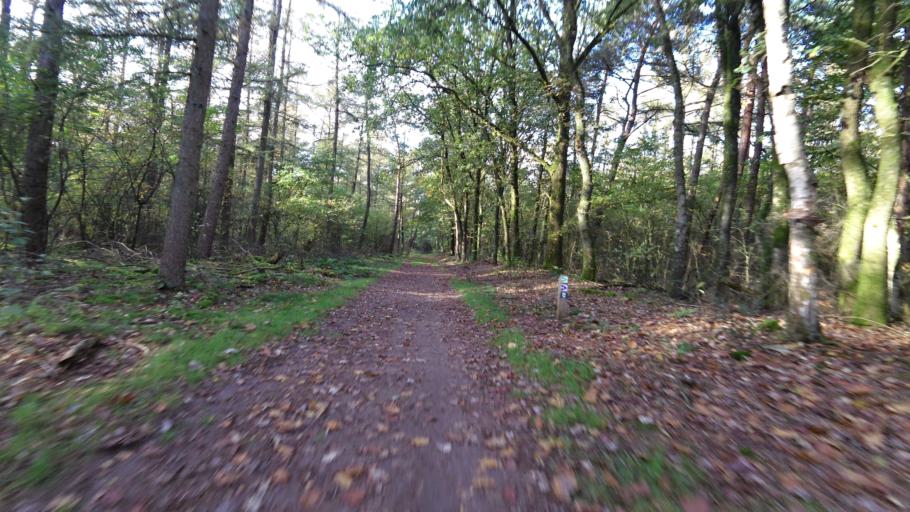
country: NL
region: Gelderland
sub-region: Gemeente Ede
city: Ede
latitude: 52.0592
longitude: 5.6621
